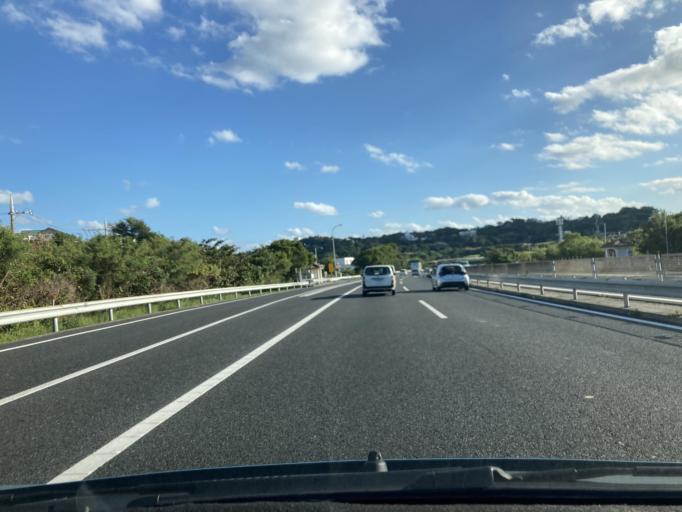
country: JP
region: Okinawa
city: Chatan
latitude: 26.3030
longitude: 127.7917
